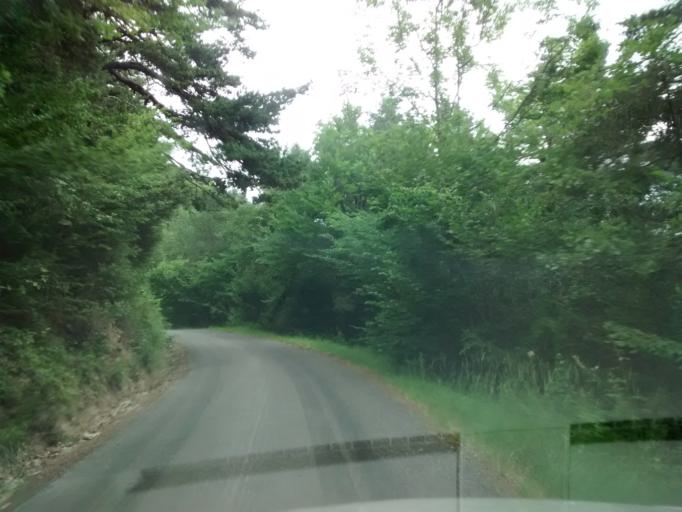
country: ES
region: Aragon
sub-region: Provincia de Huesca
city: Puertolas
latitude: 42.5704
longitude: 0.1394
